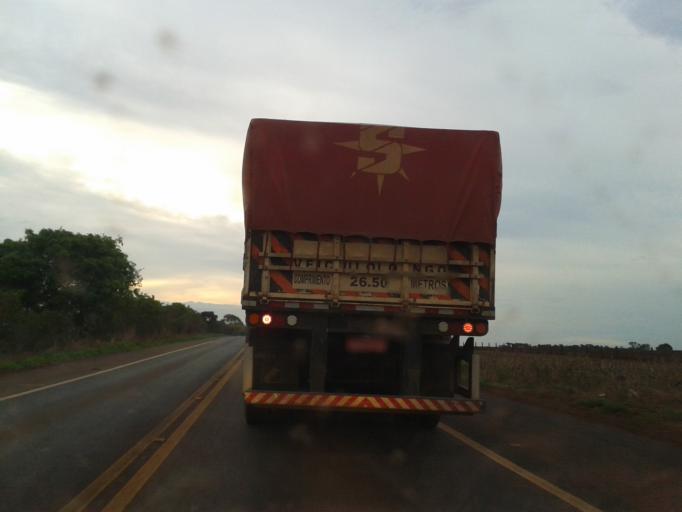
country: BR
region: Goias
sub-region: Santa Helena De Goias
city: Santa Helena de Goias
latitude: -17.9457
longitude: -50.5158
